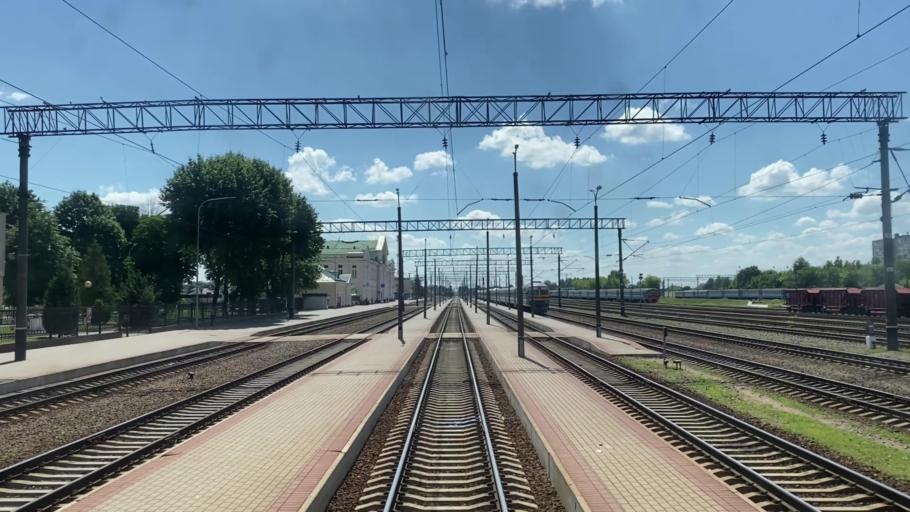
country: BY
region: Brest
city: Baranovichi
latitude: 53.1310
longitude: 26.0403
